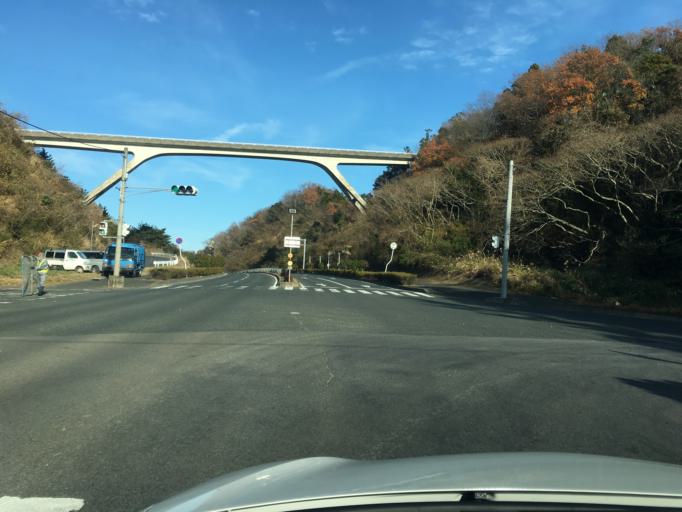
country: JP
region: Fukushima
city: Iwaki
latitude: 36.9455
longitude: 140.9190
